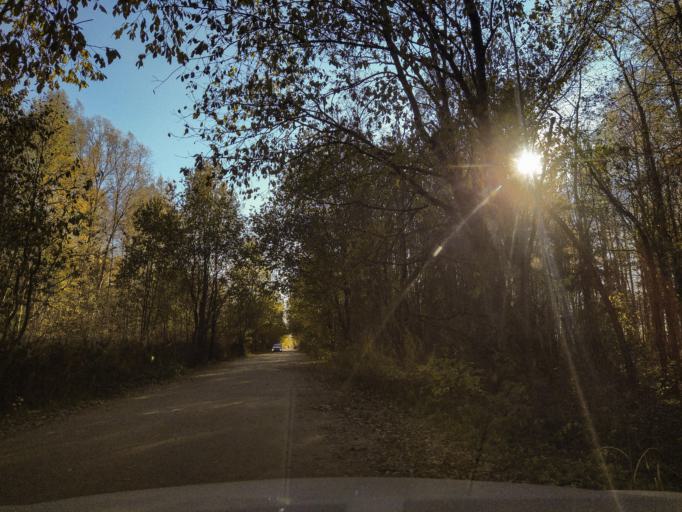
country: RU
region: Leningrad
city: Siverskiy
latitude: 59.2981
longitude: 30.0346
